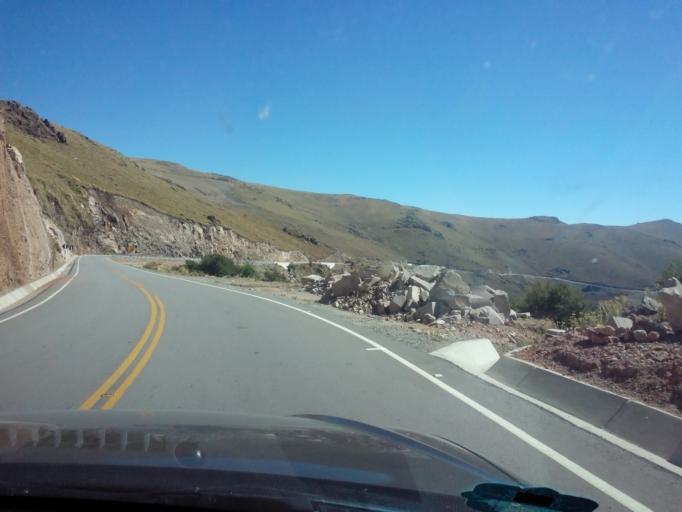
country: PE
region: Ayacucho
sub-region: Provincia de Huamanga
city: Ocros
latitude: -13.3935
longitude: -73.9501
